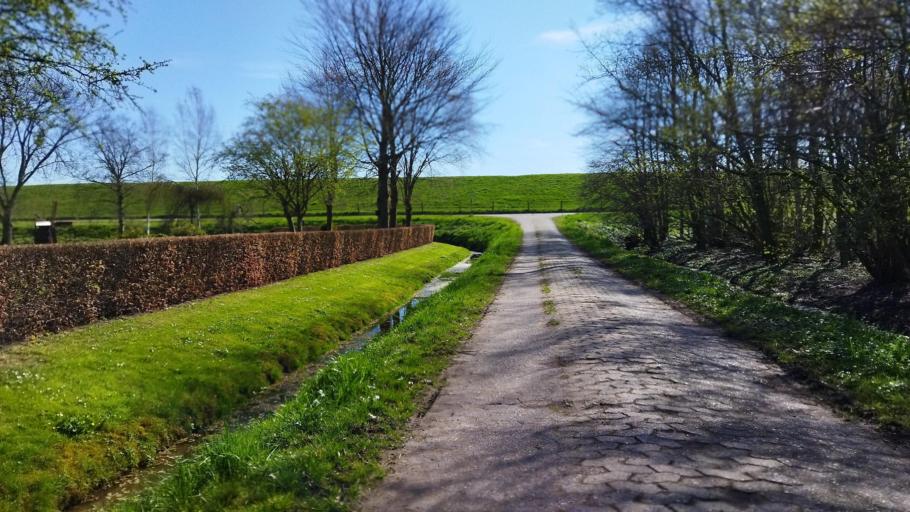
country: DE
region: Lower Saxony
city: Elsfleth
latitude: 53.2136
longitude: 8.4447
